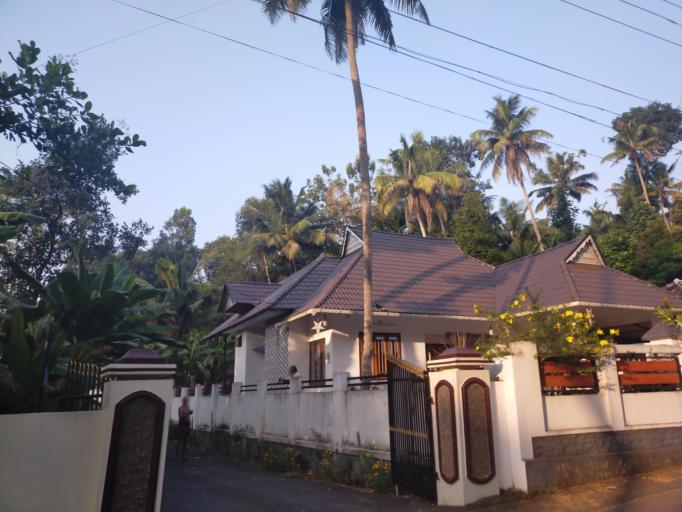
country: IN
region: Kerala
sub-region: Kottayam
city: Vaikam
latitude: 9.7515
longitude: 76.5049
